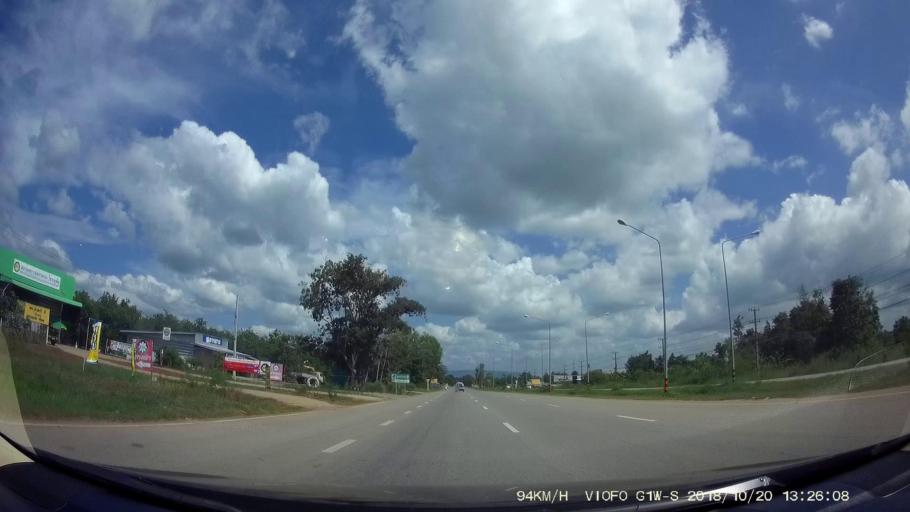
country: TH
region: Chaiyaphum
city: Khon San
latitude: 16.5942
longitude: 101.9418
